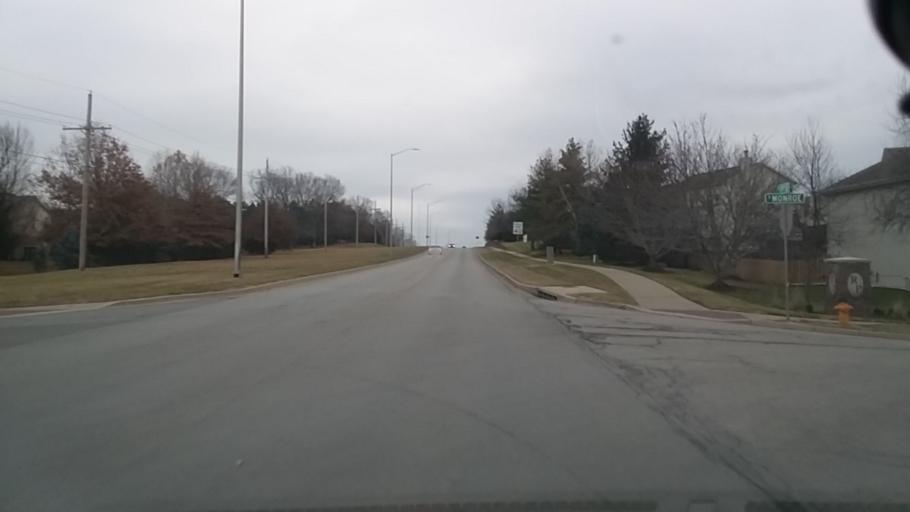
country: US
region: Kansas
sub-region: Johnson County
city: Olathe
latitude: 38.9127
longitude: -94.8294
